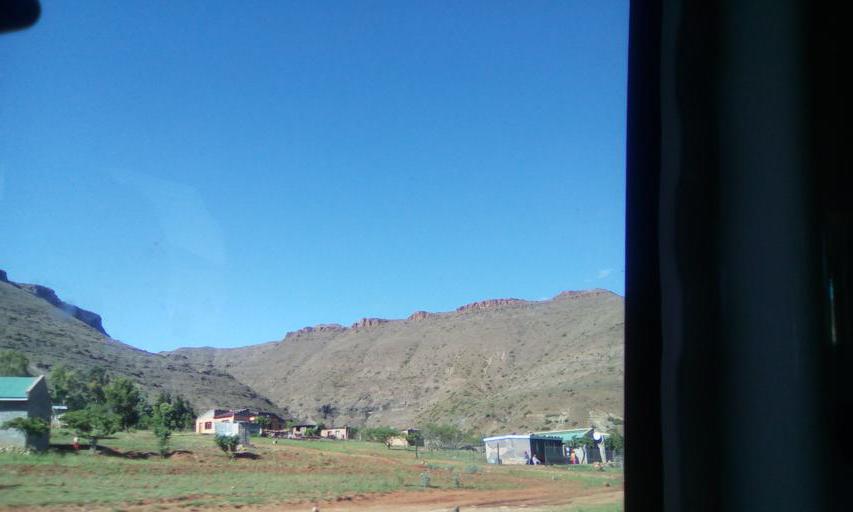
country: LS
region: Qacha's Nek
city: Qacha's Nek
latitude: -30.0581
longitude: 28.2880
